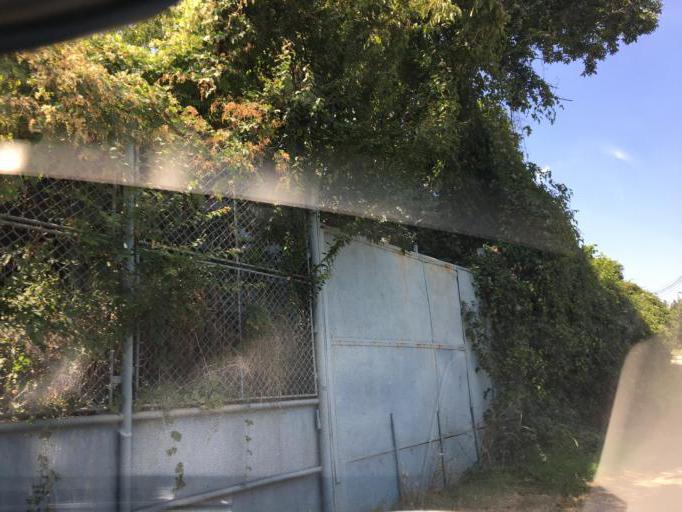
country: BG
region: Sofiya
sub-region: Obshtina Elin Pelin
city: Elin Pelin
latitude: 42.6022
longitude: 23.4698
